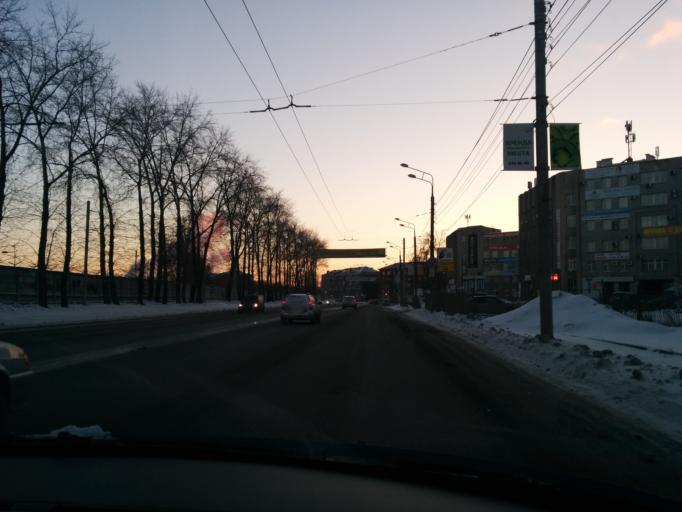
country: RU
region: Perm
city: Perm
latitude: 57.9946
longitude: 56.2594
